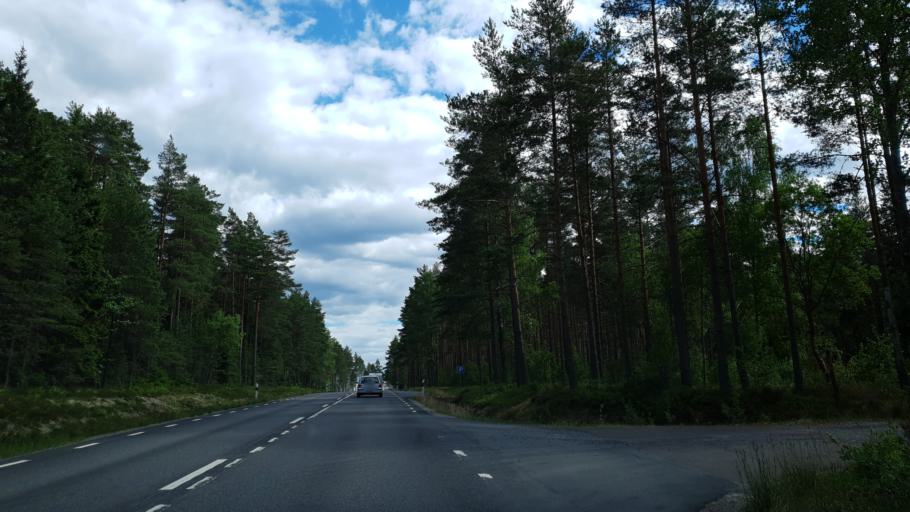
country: SE
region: Kronoberg
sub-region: Lessebo Kommun
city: Lessebo
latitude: 56.8212
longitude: 15.4075
